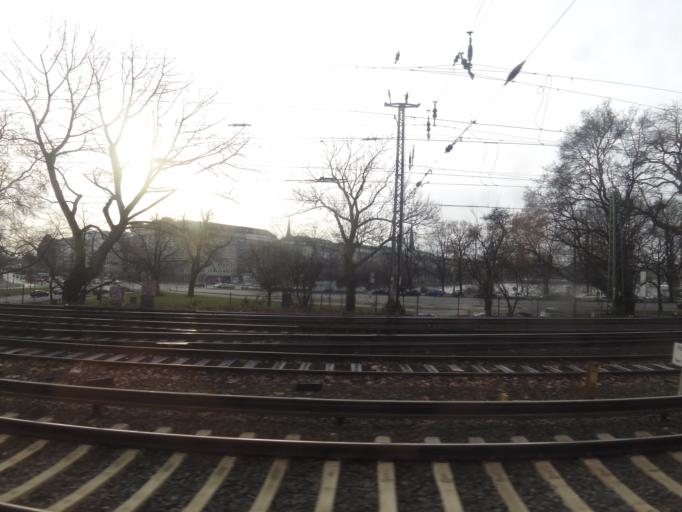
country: DE
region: Hamburg
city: Altstadt
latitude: 53.5568
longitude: 9.9999
